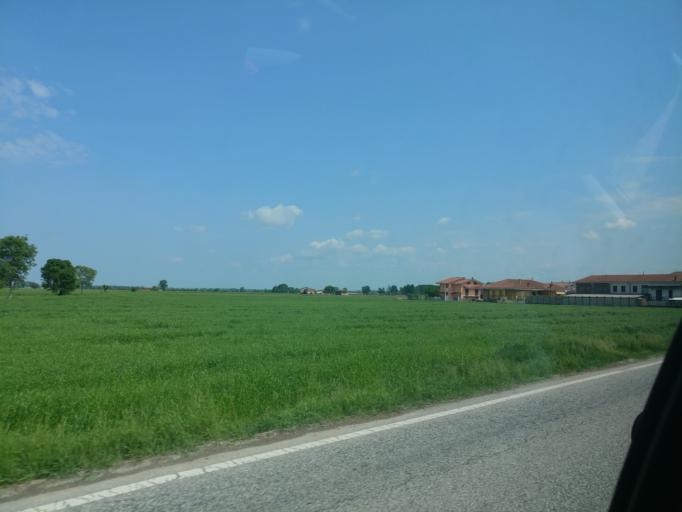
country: IT
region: Piedmont
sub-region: Provincia di Torino
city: Cavour
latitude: 44.7522
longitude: 7.4054
